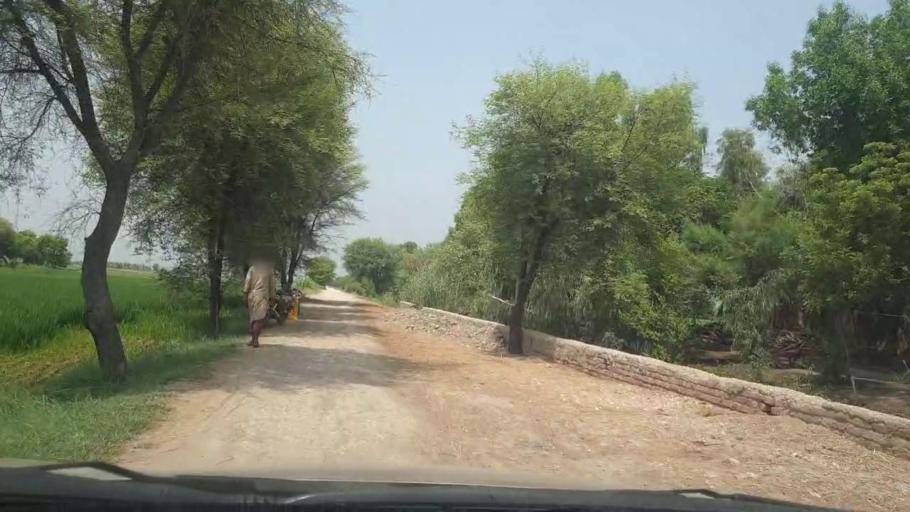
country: PK
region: Sindh
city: Naudero
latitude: 27.6884
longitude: 68.2435
